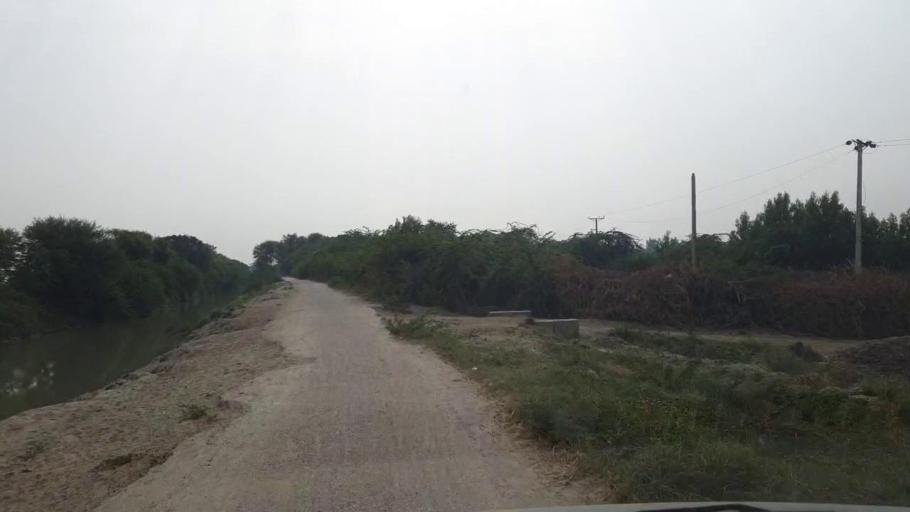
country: PK
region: Sindh
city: Matli
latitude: 25.0051
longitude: 68.7011
